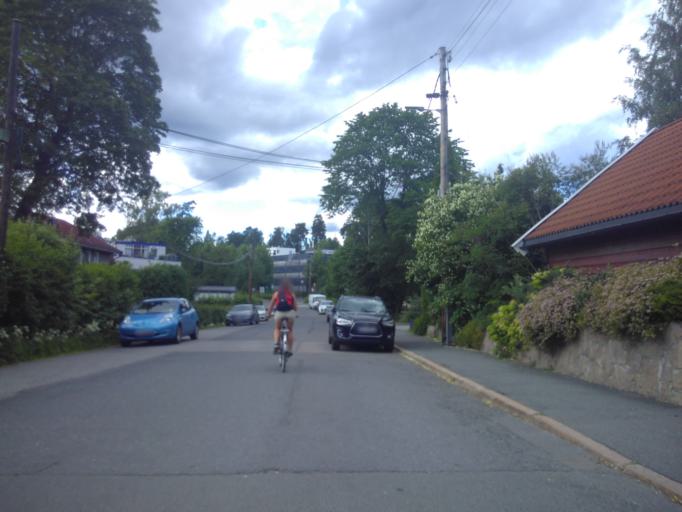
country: NO
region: Akershus
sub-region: Baerum
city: Lysaker
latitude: 59.9259
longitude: 10.6440
